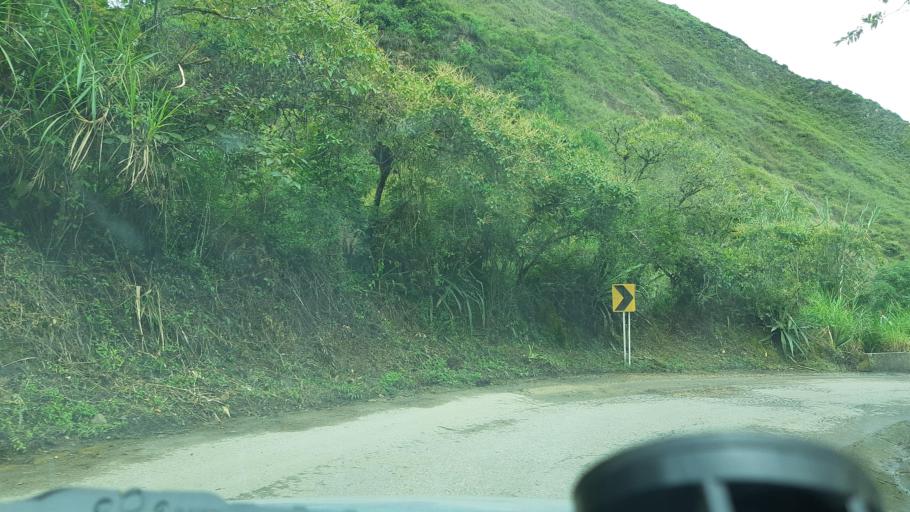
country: CO
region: Cundinamarca
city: Manta
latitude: 5.0340
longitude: -73.5169
